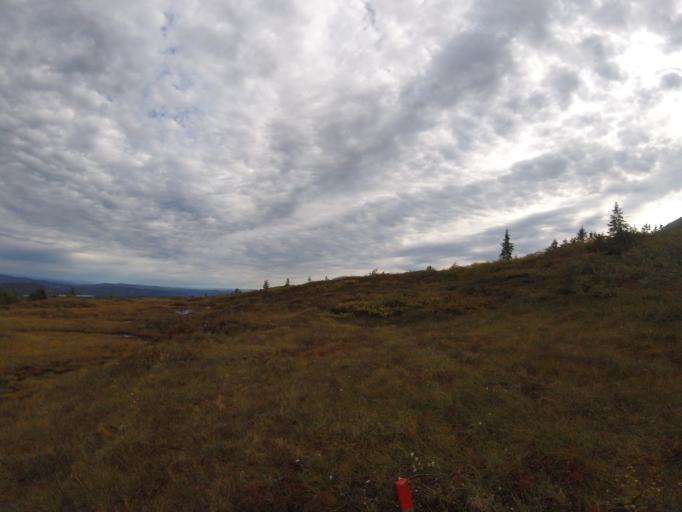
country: NO
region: Buskerud
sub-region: Rollag
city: Rollag
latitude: 59.8067
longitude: 9.3031
